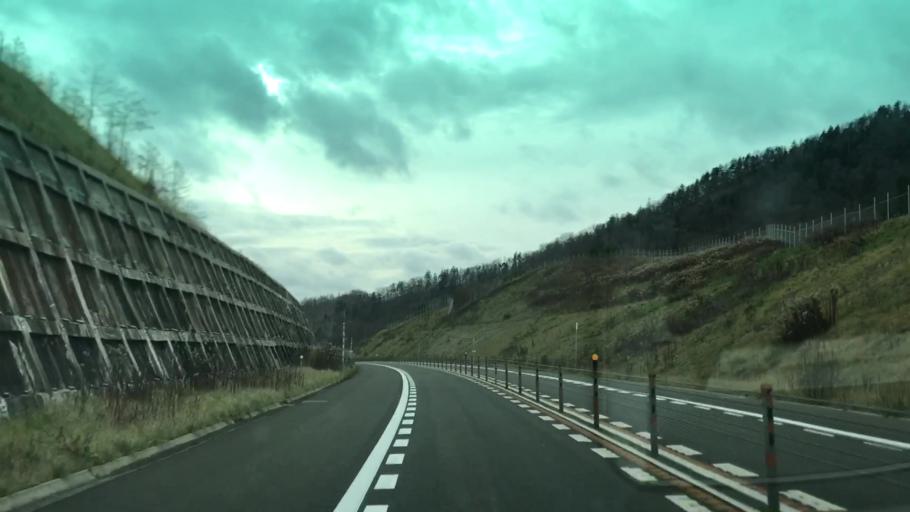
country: JP
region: Hokkaido
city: Iwamizawa
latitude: 42.9314
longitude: 142.0401
